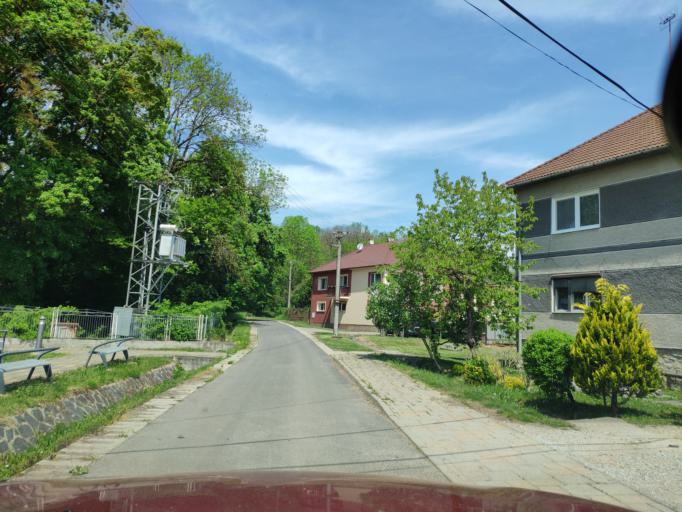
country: SK
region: Banskobystricky
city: Rimavska Sobota
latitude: 48.4483
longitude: 20.1164
